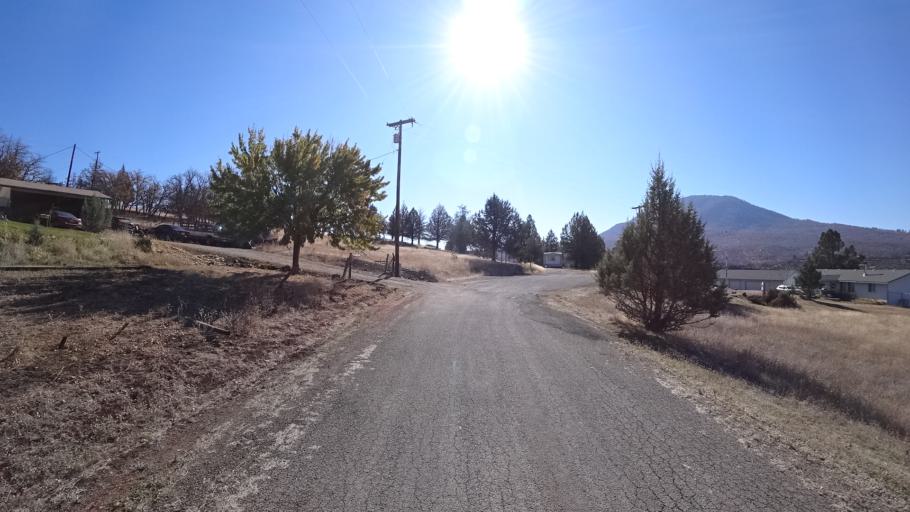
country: US
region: California
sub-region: Siskiyou County
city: Montague
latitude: 41.8994
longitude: -122.4838
